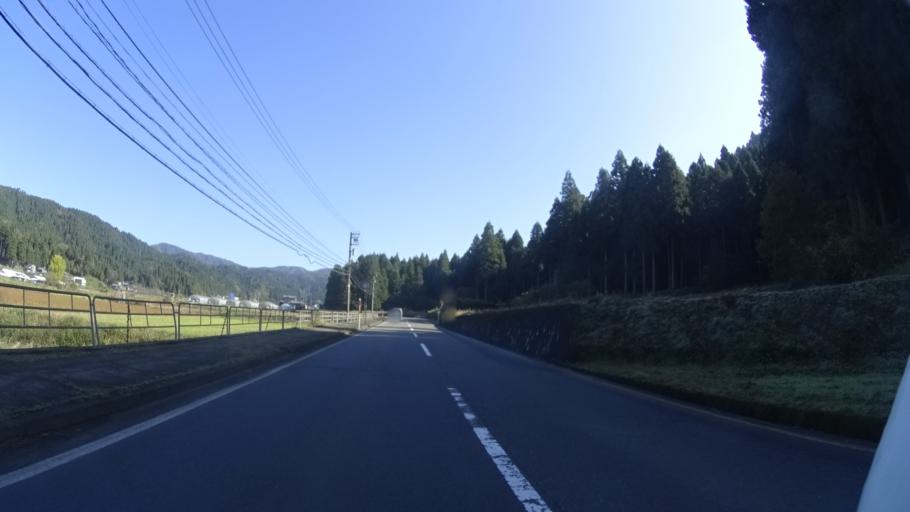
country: JP
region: Fukui
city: Sabae
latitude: 35.9354
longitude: 136.2862
